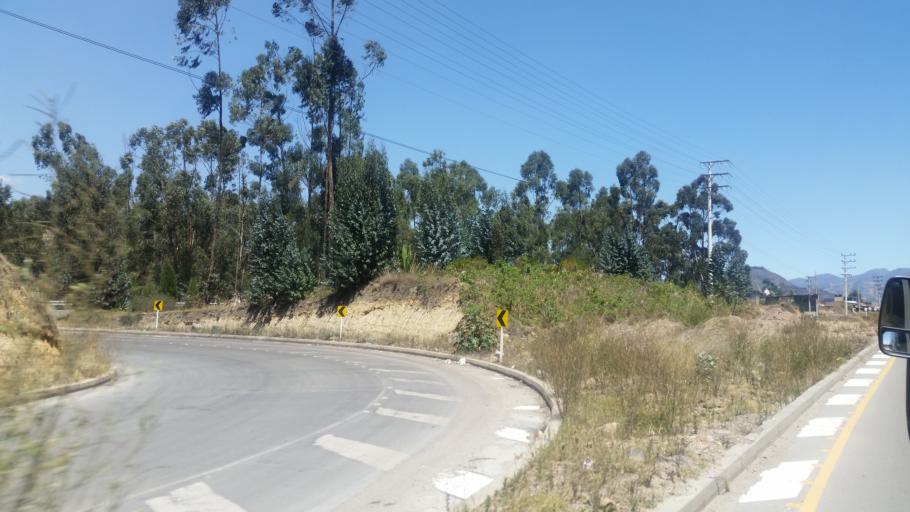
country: CO
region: Boyaca
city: Nobsa
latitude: 5.7595
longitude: -72.8878
